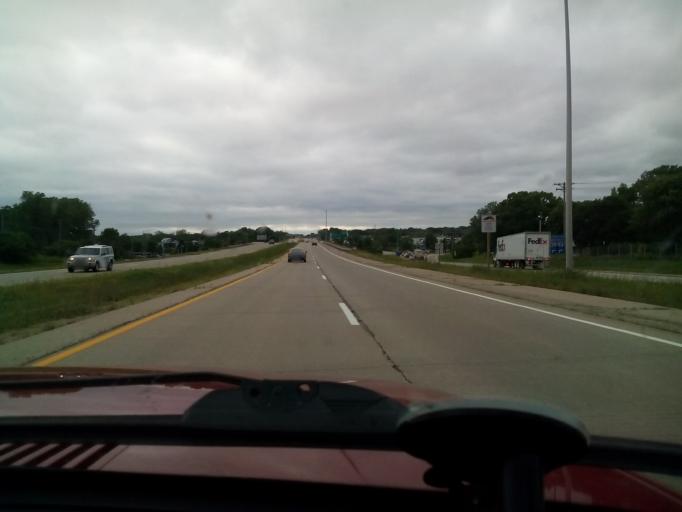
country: US
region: Wisconsin
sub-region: Dane County
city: Monona
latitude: 43.1065
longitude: -89.3121
